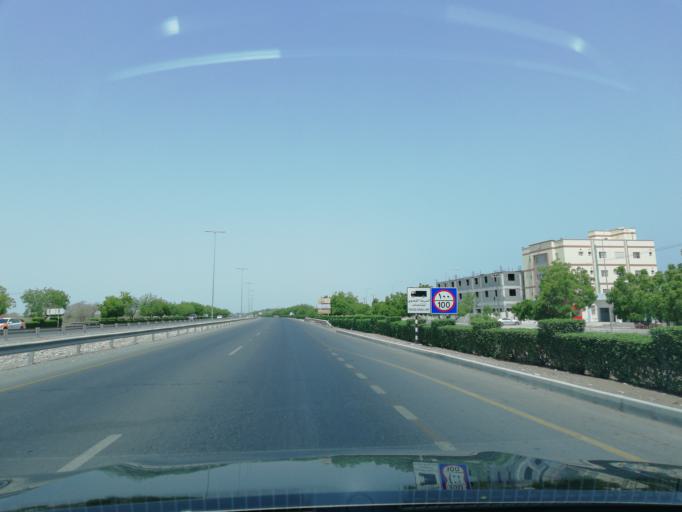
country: OM
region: Muhafazat Masqat
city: As Sib al Jadidah
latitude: 23.6934
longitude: 58.0597
